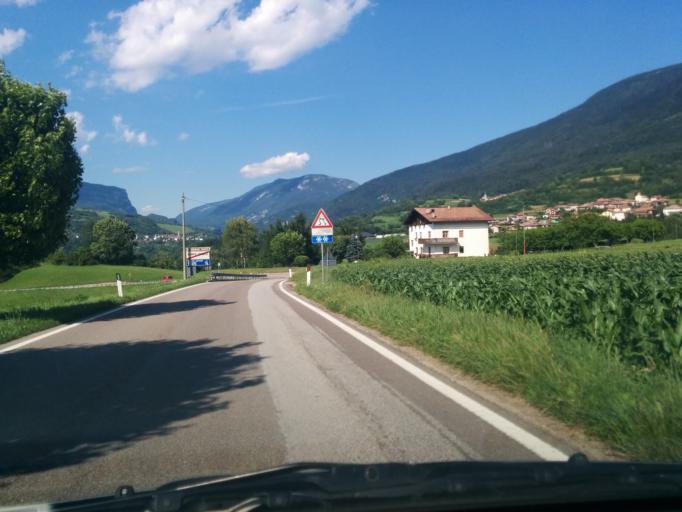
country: IT
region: Trentino-Alto Adige
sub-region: Provincia di Trento
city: Ponte Arche
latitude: 46.0262
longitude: 10.8669
